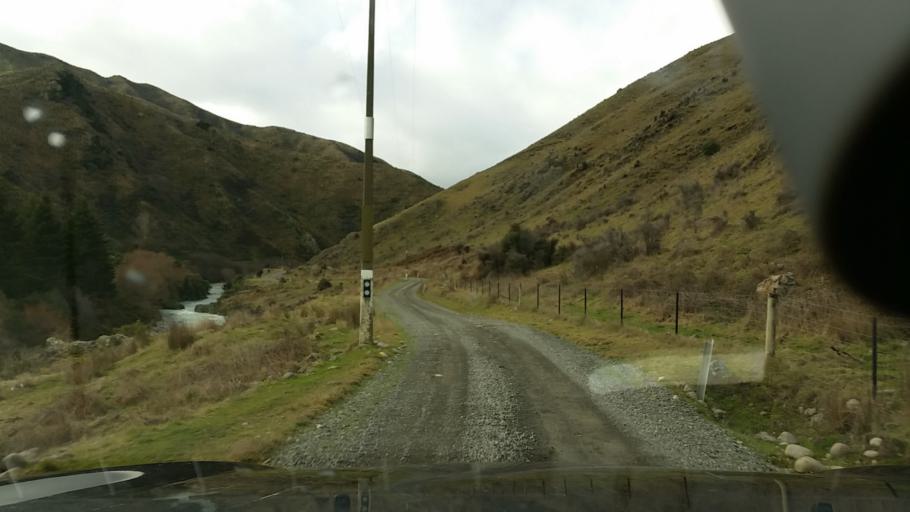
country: NZ
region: Tasman
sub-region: Tasman District
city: Richmond
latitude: -41.7314
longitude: 173.4394
